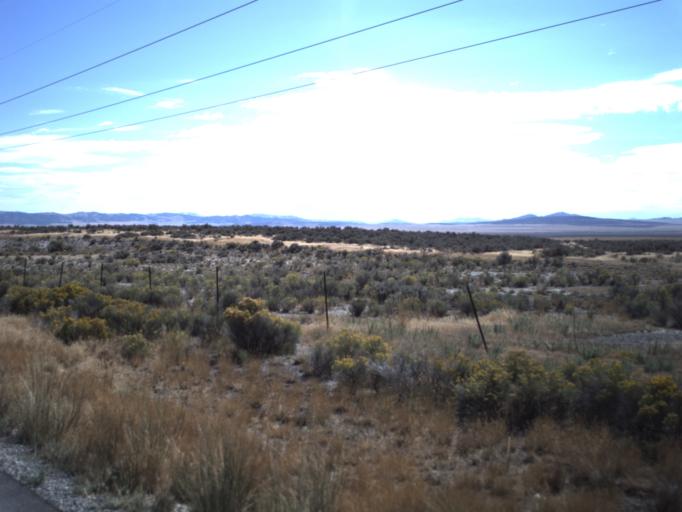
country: US
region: Idaho
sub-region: Oneida County
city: Malad City
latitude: 41.9658
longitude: -112.9981
